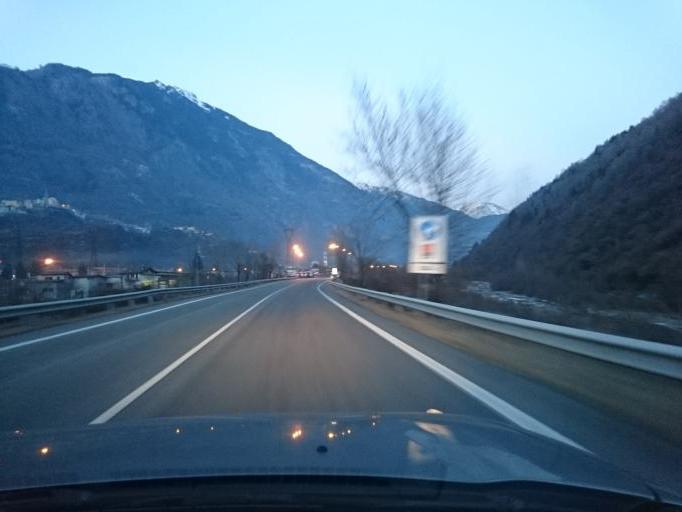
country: IT
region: Lombardy
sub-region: Provincia di Sondrio
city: Grosotto
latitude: 46.2862
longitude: 10.2674
